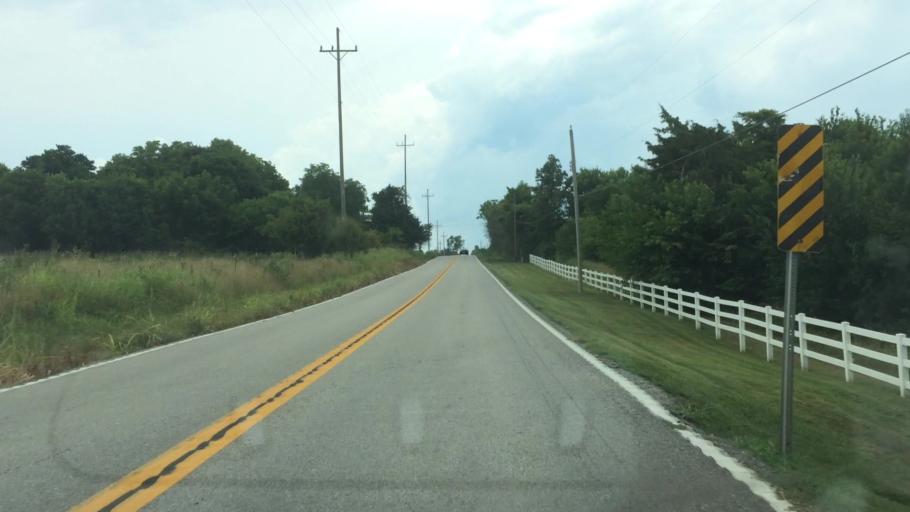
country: US
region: Missouri
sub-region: Greene County
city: Strafford
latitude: 37.2575
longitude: -93.1352
